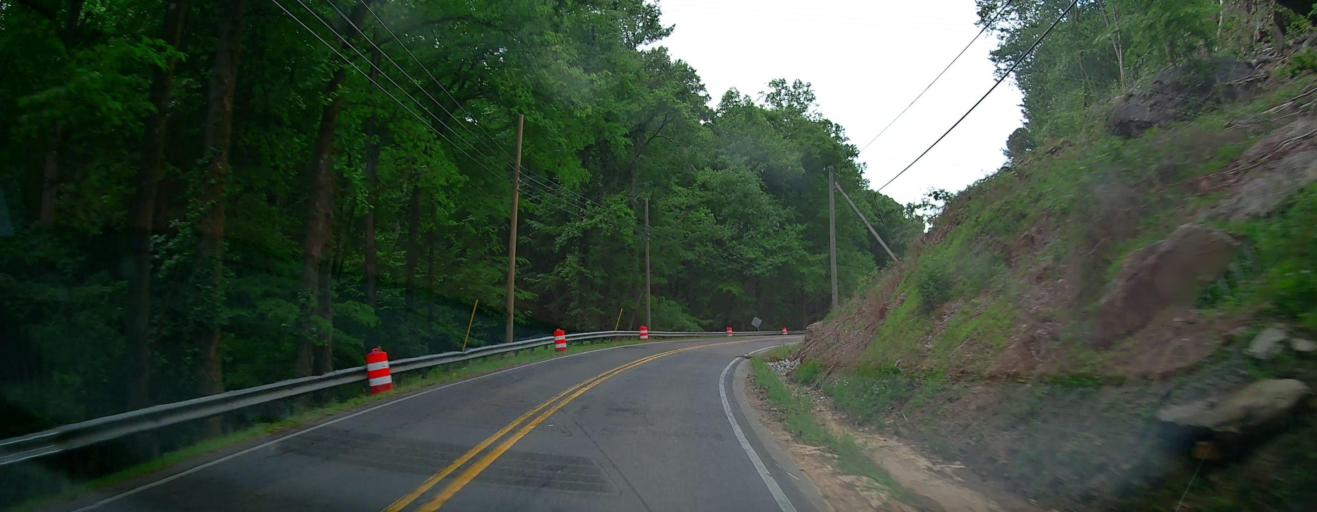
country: US
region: Alabama
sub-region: Jefferson County
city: Irondale
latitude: 33.5281
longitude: -86.6700
